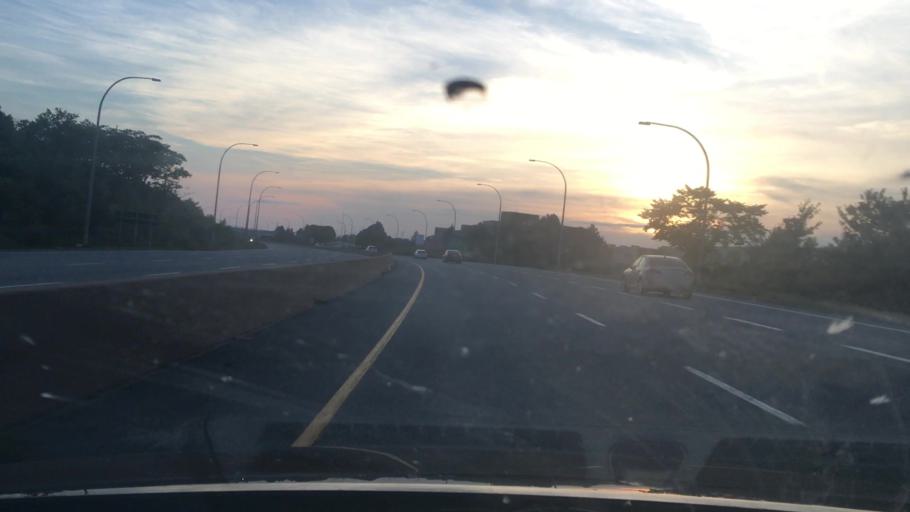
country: CA
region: Nova Scotia
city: Dartmouth
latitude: 44.6943
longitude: -63.5737
